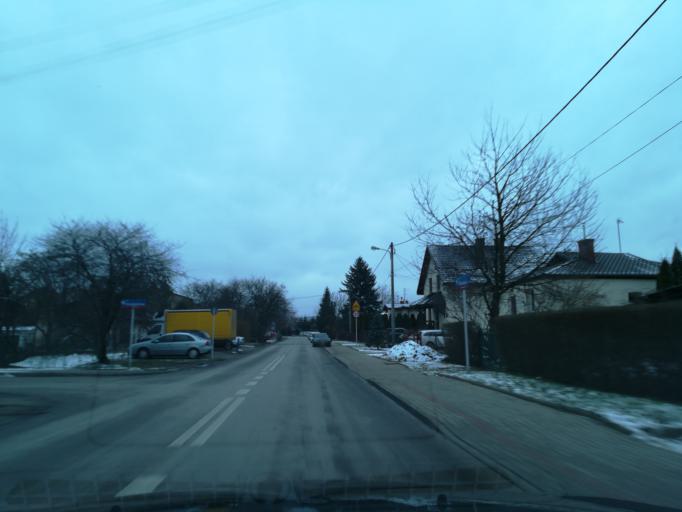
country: PL
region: Subcarpathian Voivodeship
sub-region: Rzeszow
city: Rzeszow
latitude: 50.0304
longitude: 22.0264
